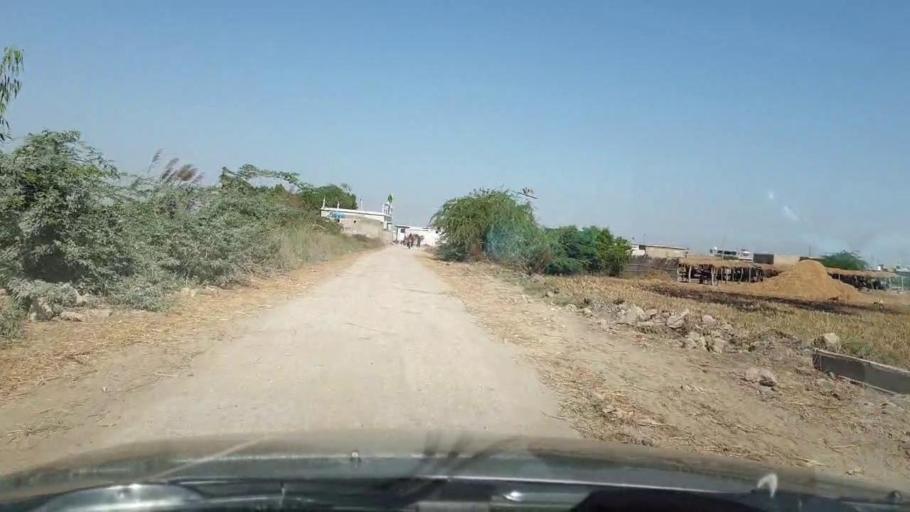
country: PK
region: Sindh
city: Thatta
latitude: 24.6348
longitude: 67.8939
